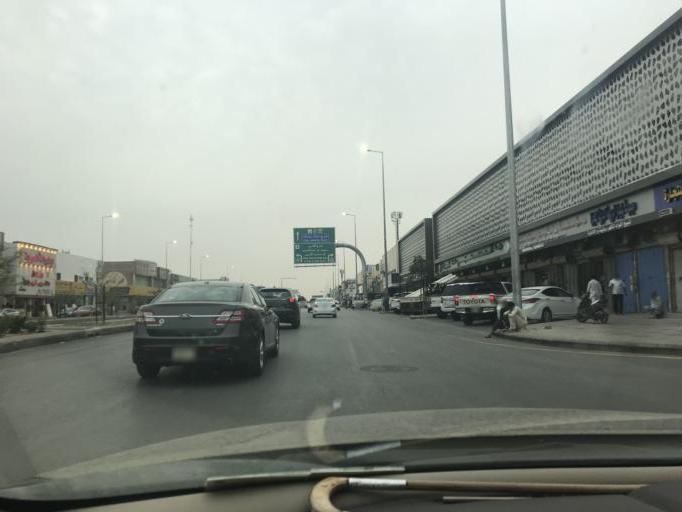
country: SA
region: Ar Riyad
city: Riyadh
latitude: 24.7605
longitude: 46.7647
